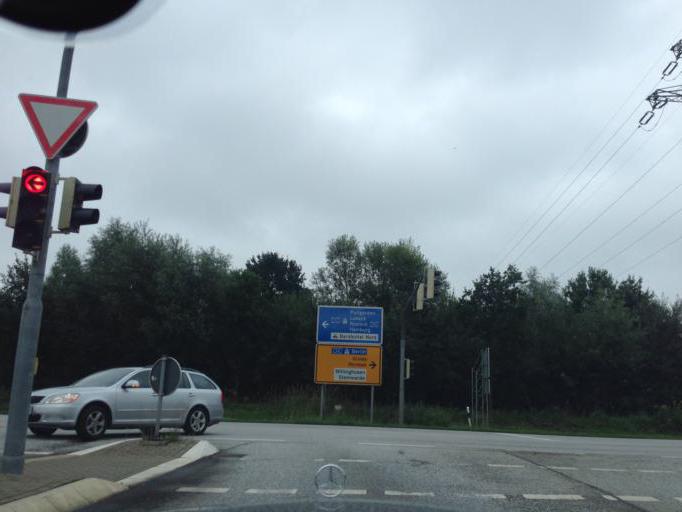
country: DE
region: Schleswig-Holstein
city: Glinde
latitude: 53.5691
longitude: 10.2001
